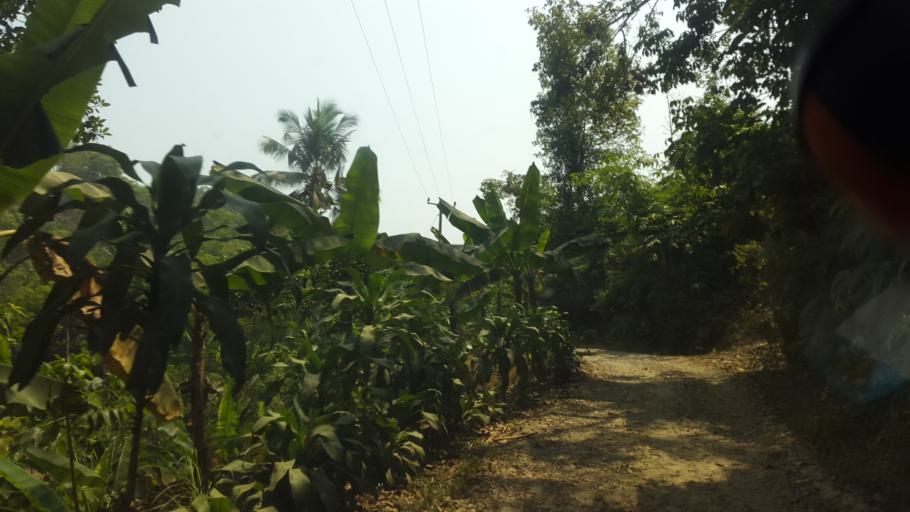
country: ID
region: West Java
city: Sindangsari
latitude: -6.9554
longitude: 106.6749
